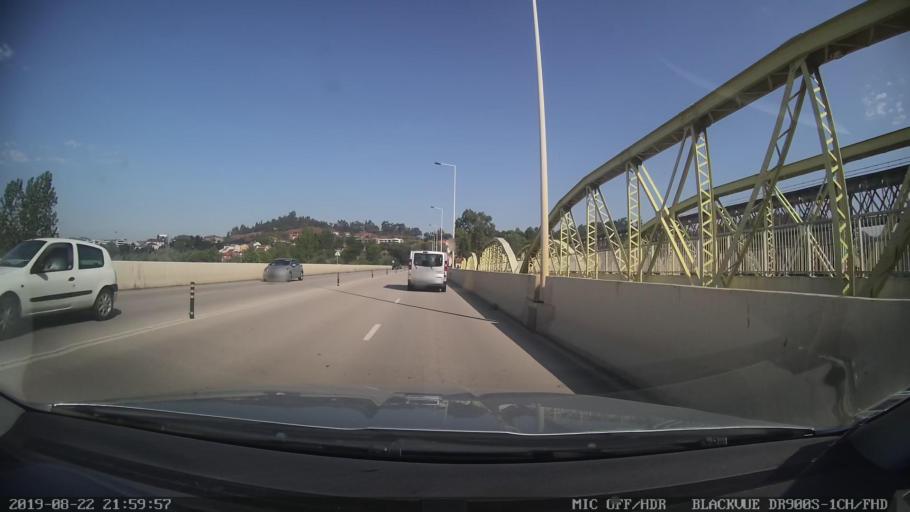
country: PT
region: Coimbra
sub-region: Coimbra
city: Coimbra
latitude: 40.1835
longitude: -8.3955
